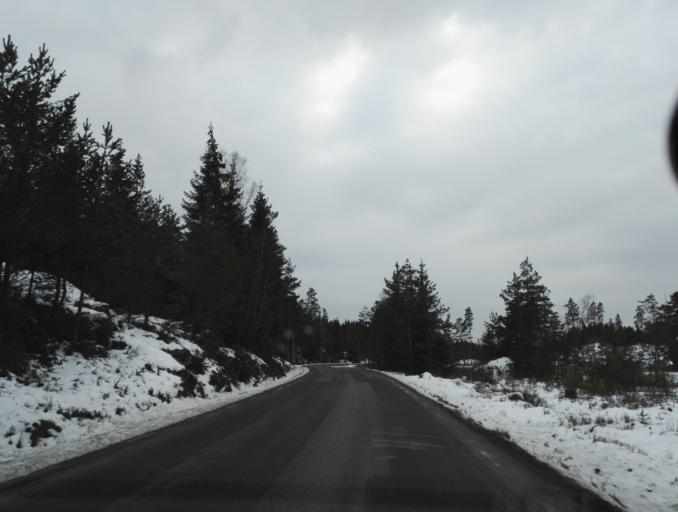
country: SE
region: Vaestra Goetaland
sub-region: Alingsas Kommun
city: Ingared
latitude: 57.7942
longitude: 12.5231
